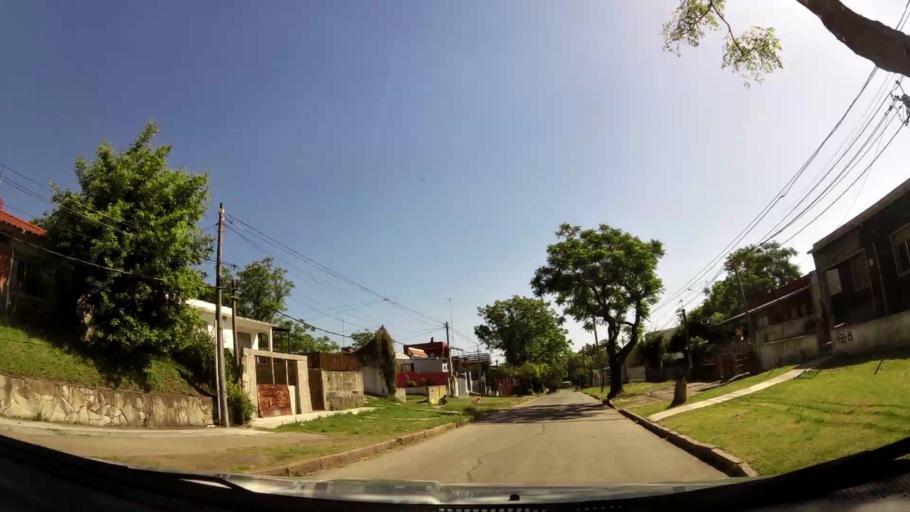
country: UY
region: Montevideo
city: Montevideo
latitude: -34.8533
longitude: -56.2380
